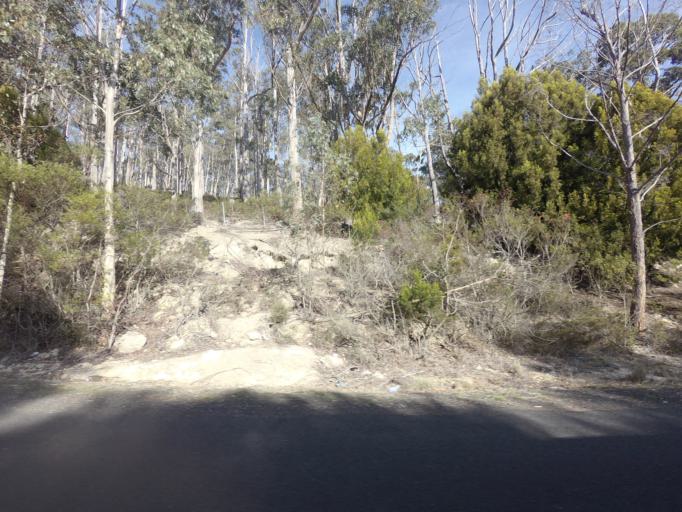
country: AU
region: Tasmania
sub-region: Sorell
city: Sorell
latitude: -42.4862
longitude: 147.4468
